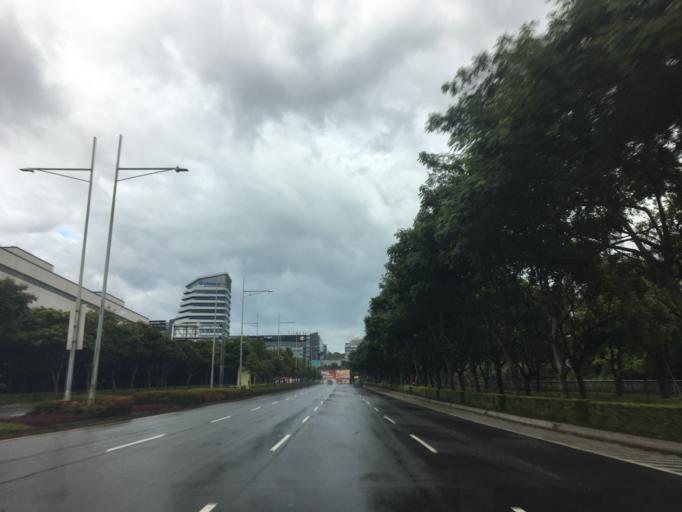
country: TW
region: Taiwan
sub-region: Taichung City
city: Taichung
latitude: 24.2093
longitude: 120.6158
